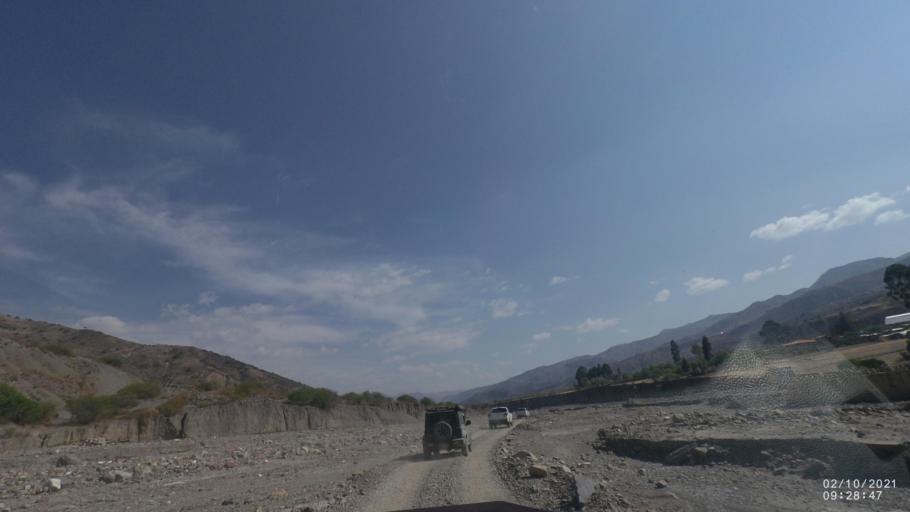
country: BO
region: Cochabamba
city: Irpa Irpa
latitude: -17.8520
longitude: -66.3186
